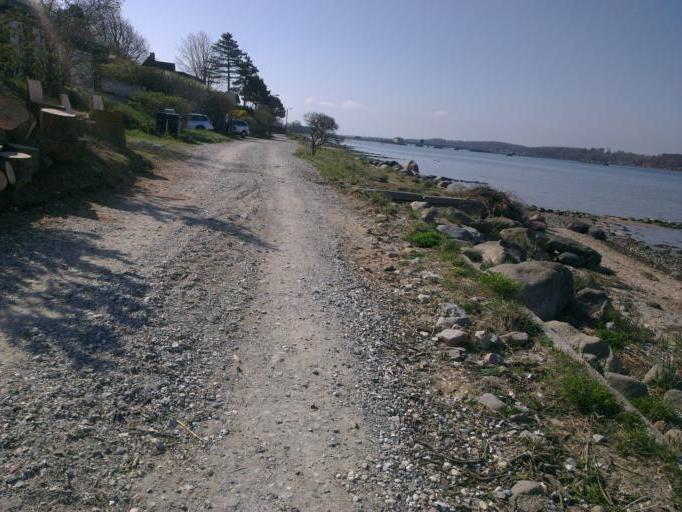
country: DK
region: Capital Region
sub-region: Frederikssund Kommune
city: Frederikssund
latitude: 55.8511
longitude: 12.0443
